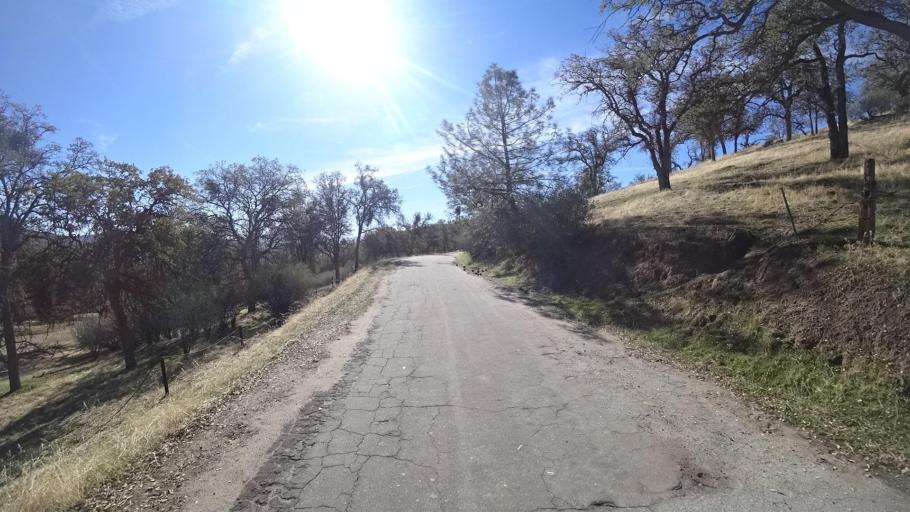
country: US
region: California
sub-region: Kern County
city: Bodfish
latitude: 35.4476
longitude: -118.6677
